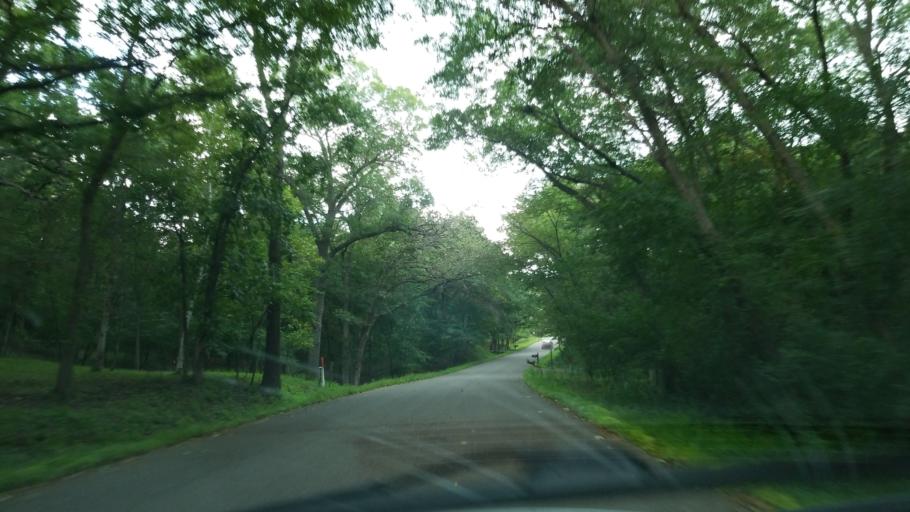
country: US
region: Minnesota
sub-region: Washington County
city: Afton
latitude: 44.8826
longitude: -92.7610
